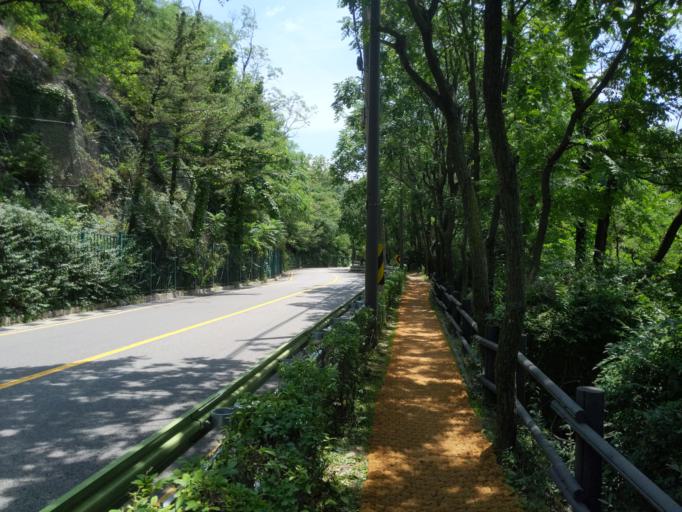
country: KR
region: Seoul
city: Seoul
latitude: 37.5995
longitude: 126.9728
